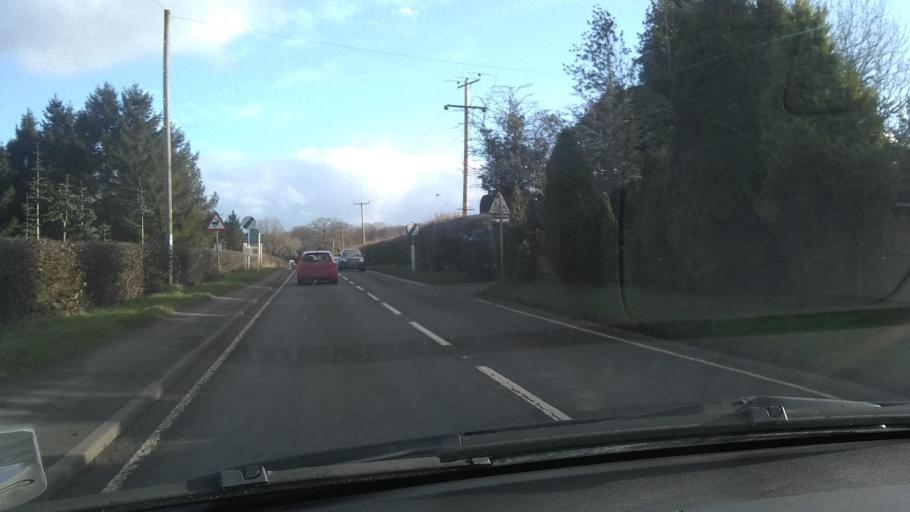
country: GB
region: England
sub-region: Worcestershire
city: Bewdley
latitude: 52.3673
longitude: -2.3974
